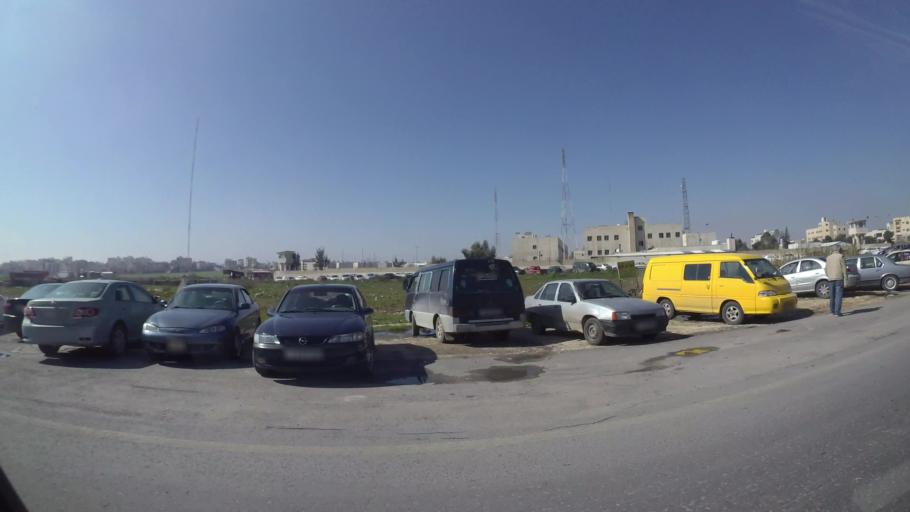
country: JO
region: Amman
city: Al Bunayyat ash Shamaliyah
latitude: 31.9059
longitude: 35.8860
